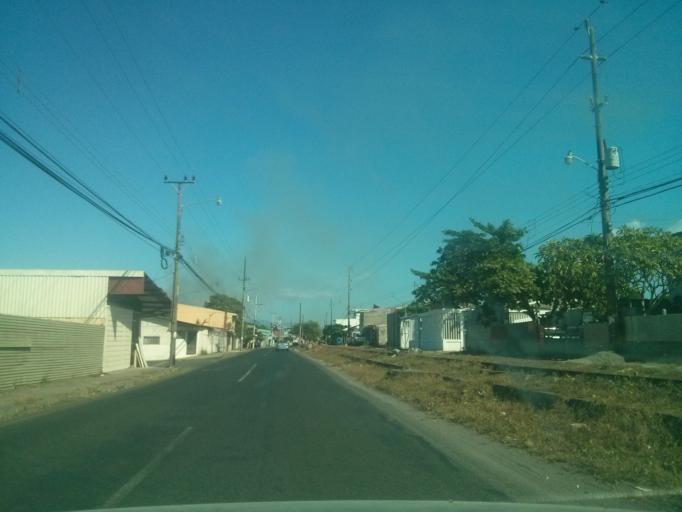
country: CR
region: Puntarenas
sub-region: Canton Central de Puntarenas
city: Chacarita
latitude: 9.9810
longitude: -84.8087
